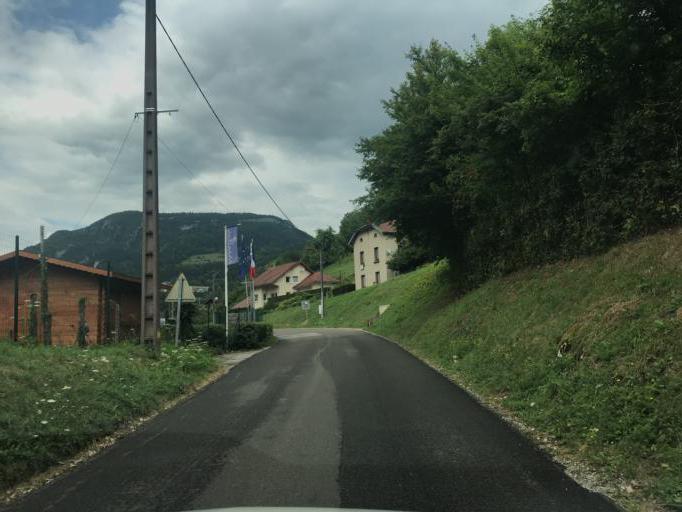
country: FR
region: Franche-Comte
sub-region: Departement du Jura
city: Saint-Claude
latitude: 46.3712
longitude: 5.8723
